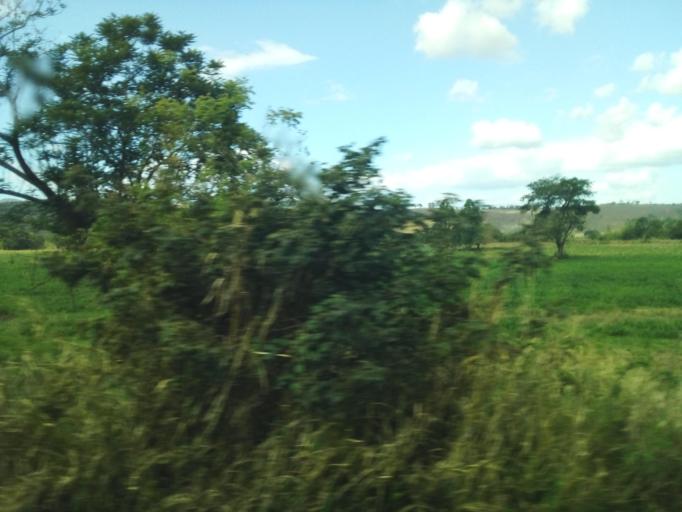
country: BR
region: Minas Gerais
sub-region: Conselheiro Pena
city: Conselheiro Pena
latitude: -18.9881
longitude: -41.6002
